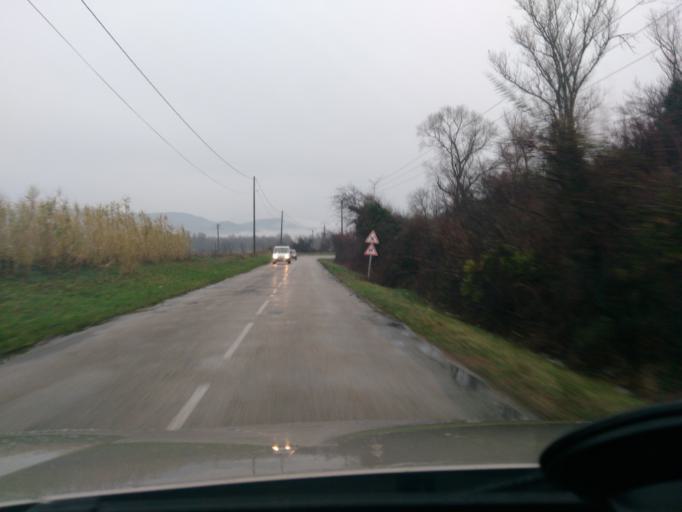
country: FR
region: Rhone-Alpes
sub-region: Departement de la Drome
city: Montelimar
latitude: 44.5408
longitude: 4.7189
